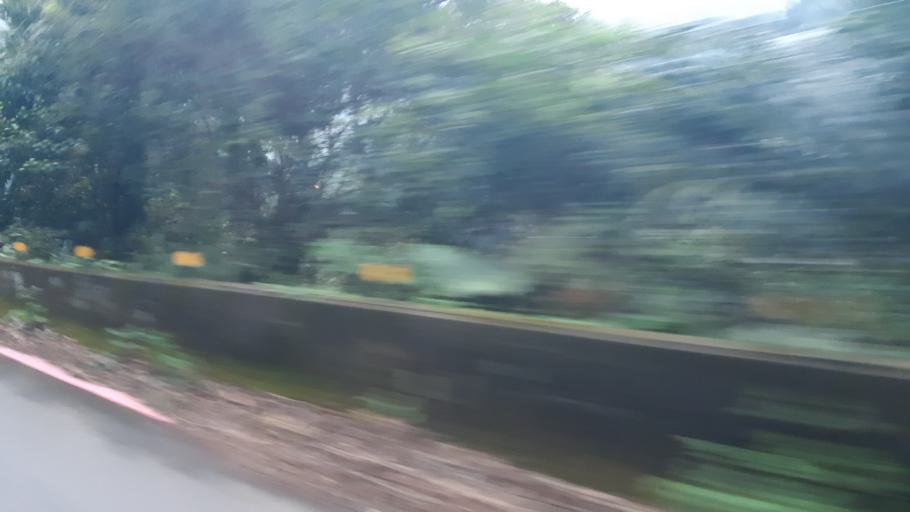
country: TW
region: Taiwan
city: Daxi
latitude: 24.6864
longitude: 121.2254
